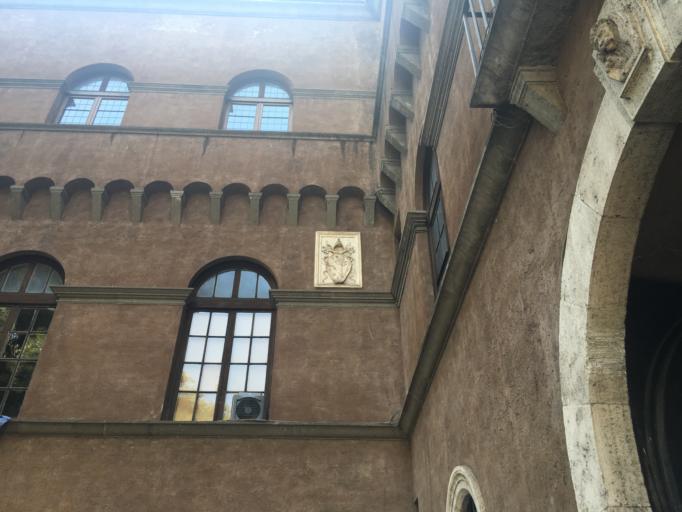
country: VA
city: Vatican City
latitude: 41.8958
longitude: 12.4815
